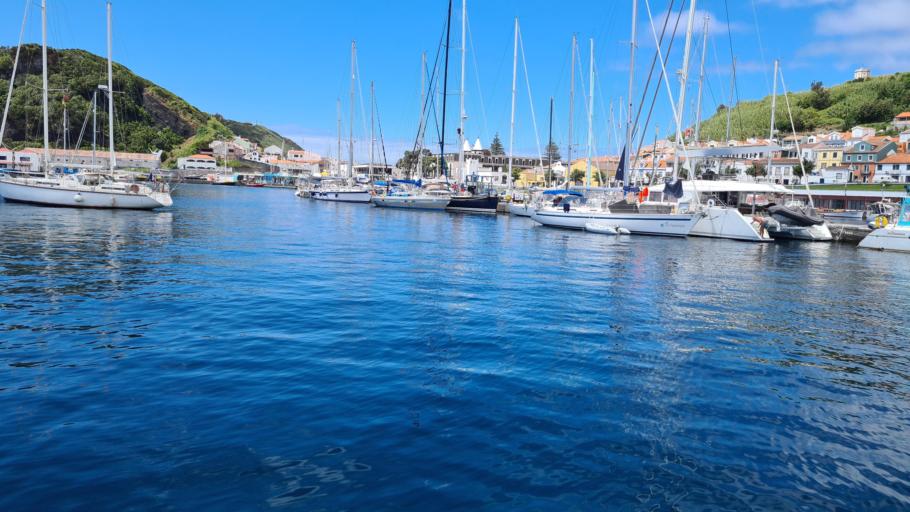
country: PT
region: Azores
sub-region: Horta
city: Horta
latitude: 38.5308
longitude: -28.6247
